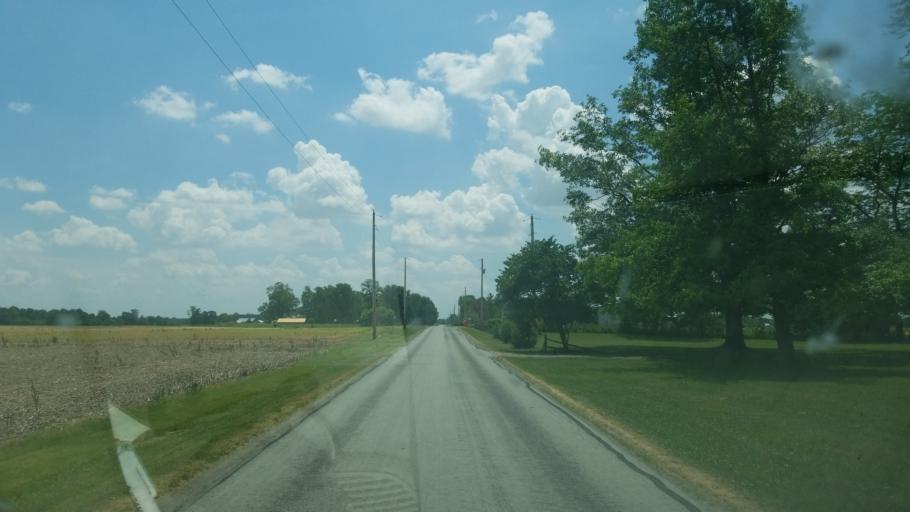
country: US
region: Ohio
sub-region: Hardin County
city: Kenton
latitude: 40.6231
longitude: -83.5603
